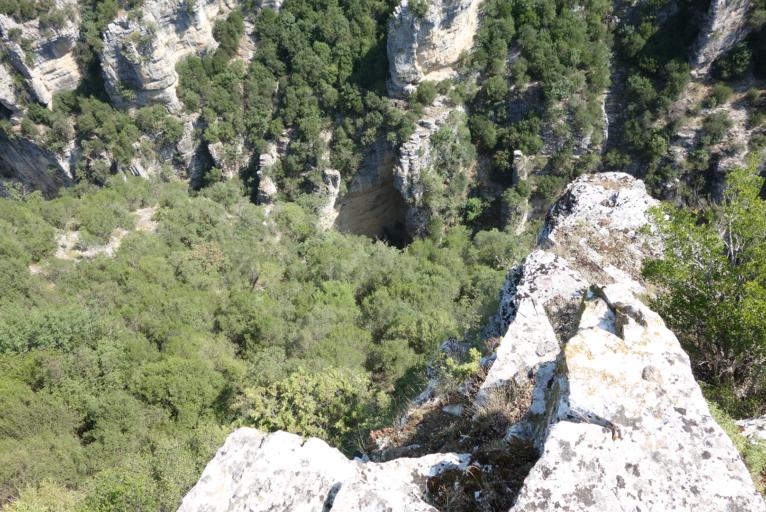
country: AL
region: Berat
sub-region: Rrethi i Skraparit
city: Corovode
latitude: 40.4855
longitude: 20.2347
